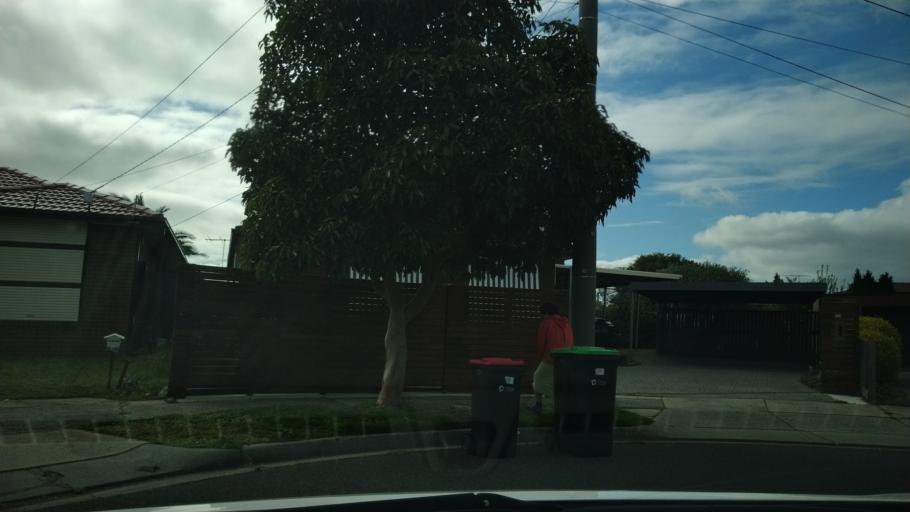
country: AU
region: Victoria
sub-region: Greater Dandenong
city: Keysborough
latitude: -37.9900
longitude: 145.1767
